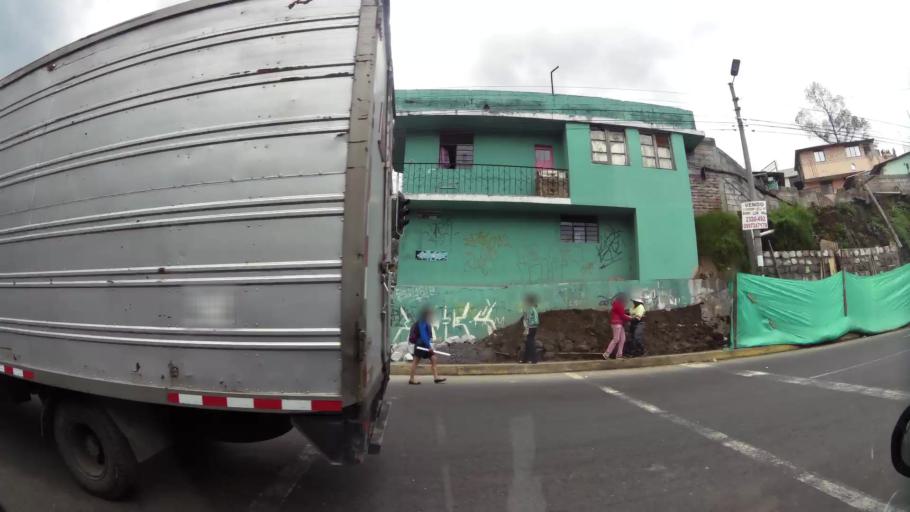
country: EC
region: Pichincha
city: Quito
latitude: -0.2411
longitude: -78.4990
